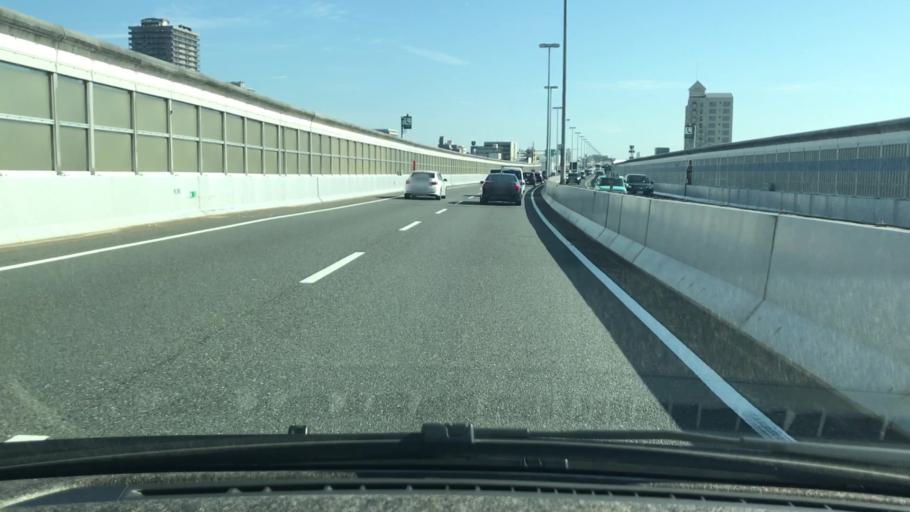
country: JP
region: Hyogo
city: Nishinomiya-hama
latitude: 34.7339
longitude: 135.3326
